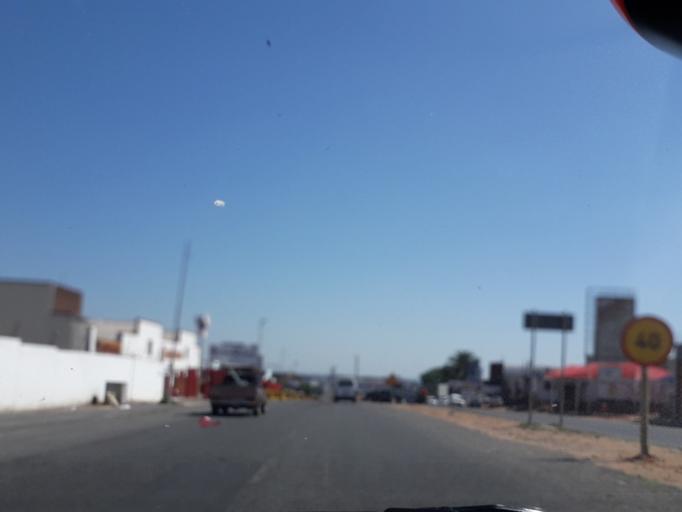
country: ZA
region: Gauteng
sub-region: City of Johannesburg Metropolitan Municipality
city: Modderfontein
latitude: -26.1146
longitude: 28.0845
